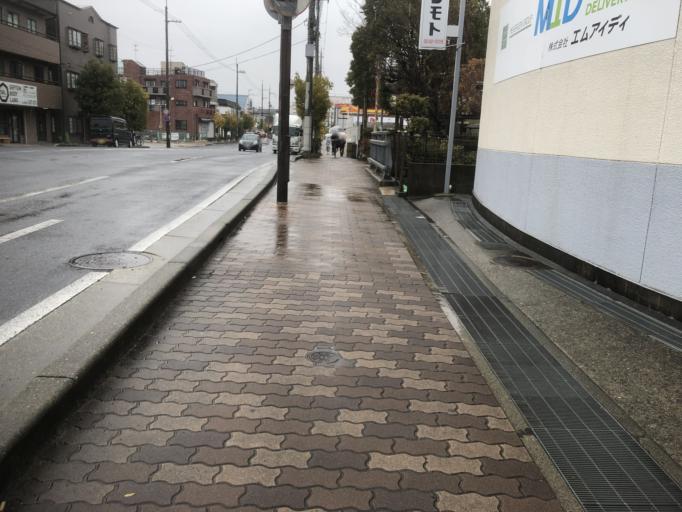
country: JP
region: Hyogo
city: Itami
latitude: 34.7551
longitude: 135.4213
